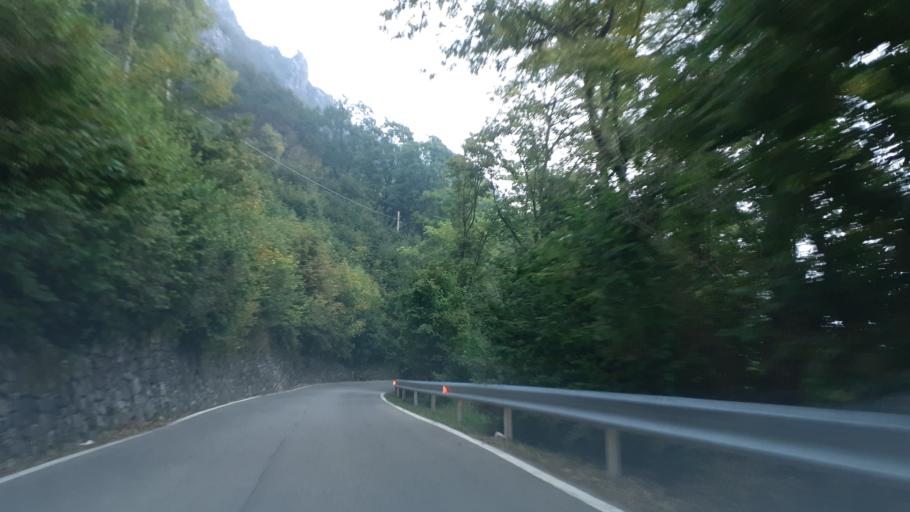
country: IT
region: Lombardy
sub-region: Provincia di Lecco
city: Ballabio
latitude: 45.9031
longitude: 9.4000
